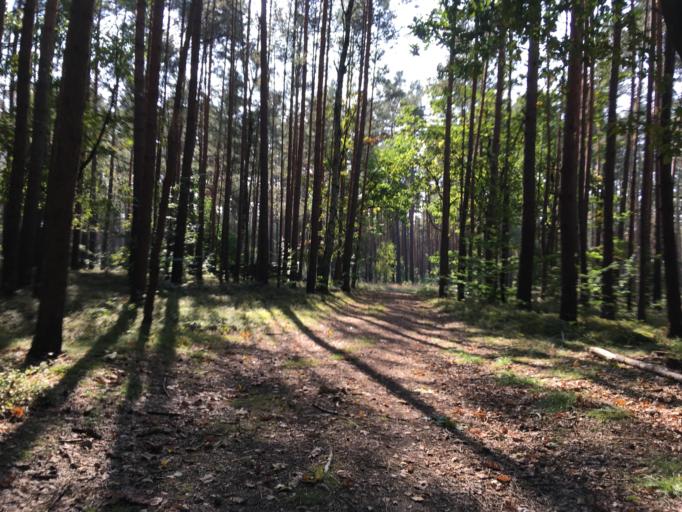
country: DE
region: Brandenburg
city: Wandlitz
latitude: 52.6939
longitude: 13.4367
